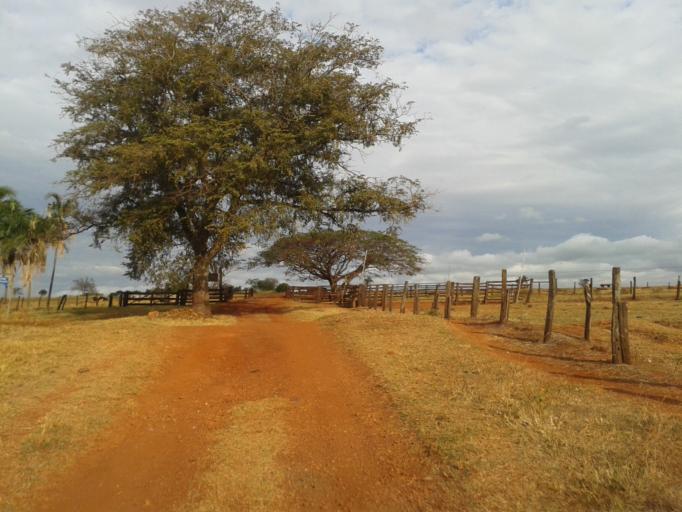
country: BR
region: Minas Gerais
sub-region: Santa Vitoria
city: Santa Vitoria
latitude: -18.7308
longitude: -50.2521
